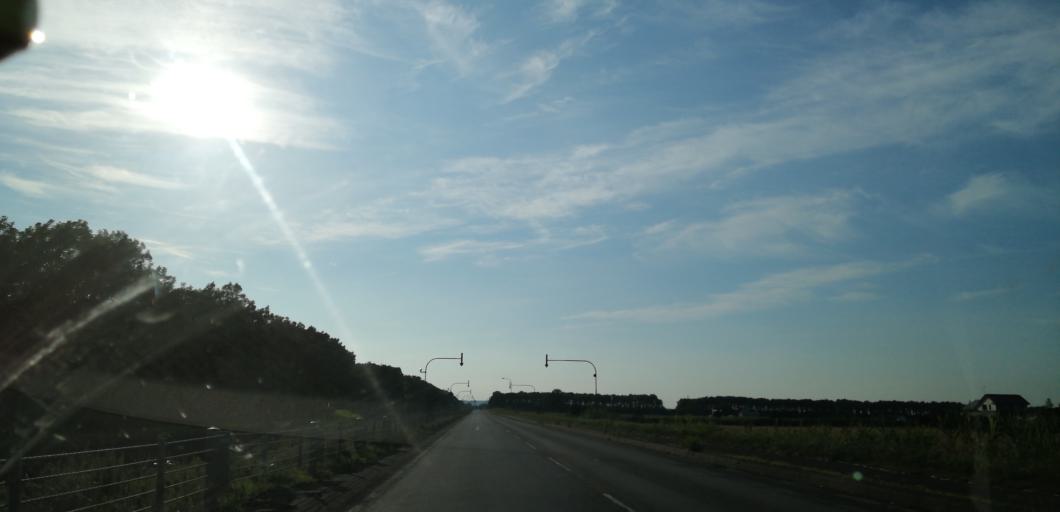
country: JP
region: Hokkaido
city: Kitahiroshima
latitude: 42.9750
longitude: 141.6494
